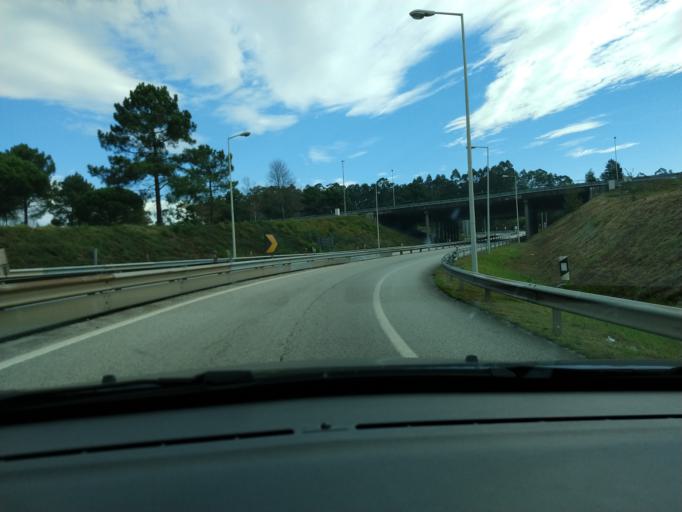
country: PT
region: Aveiro
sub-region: Albergaria-A-Velha
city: Albergaria-a-Velha
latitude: 40.6917
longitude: -8.5235
